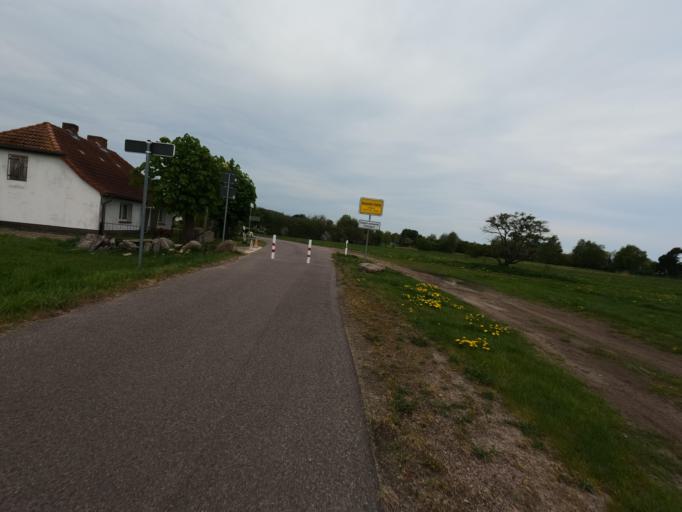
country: DE
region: Mecklenburg-Vorpommern
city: Born
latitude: 54.3438
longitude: 12.5496
